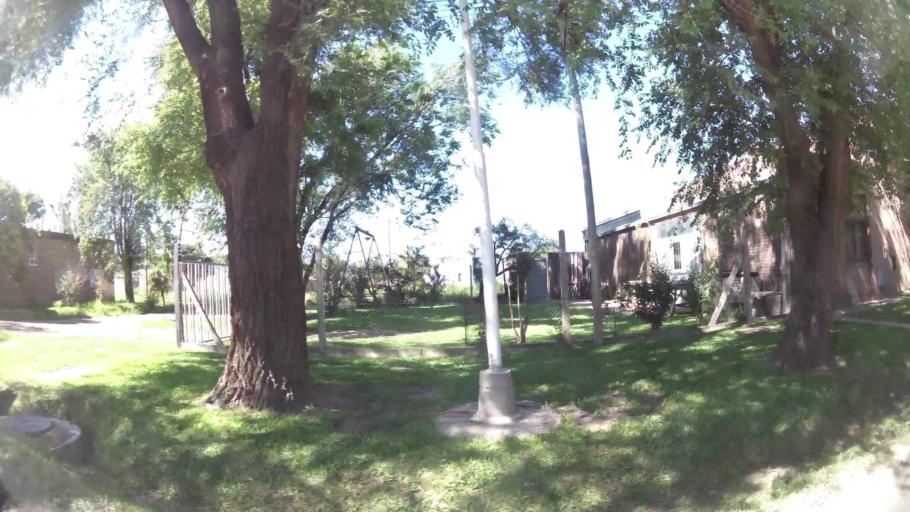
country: AR
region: Santa Fe
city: Esperanza
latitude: -31.4547
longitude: -60.9411
